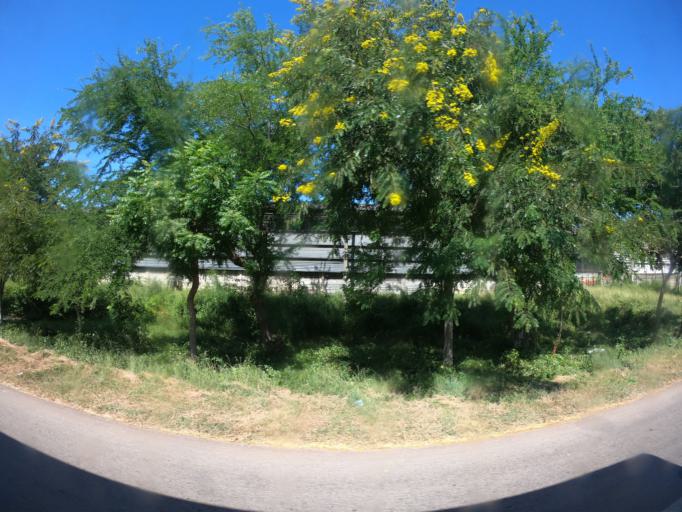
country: TH
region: Nakhon Ratchasima
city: Nakhon Ratchasima
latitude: 15.0415
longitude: 102.1489
